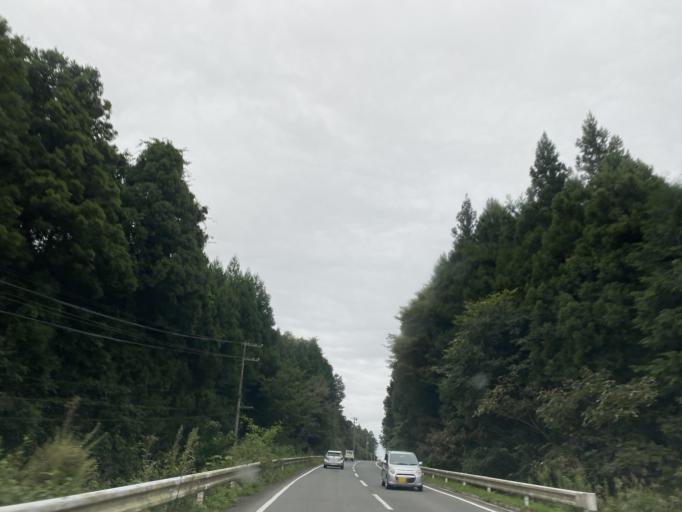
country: JP
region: Fukushima
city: Sukagawa
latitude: 37.2951
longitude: 140.2469
